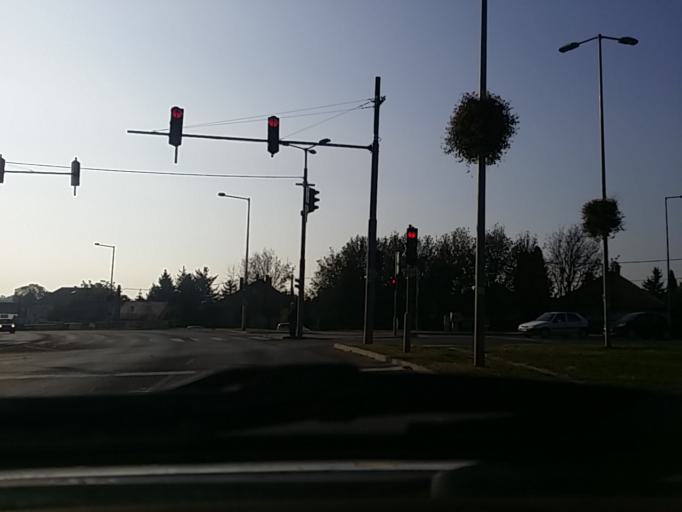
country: HU
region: Pest
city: Szentendre
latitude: 47.6648
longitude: 19.0715
